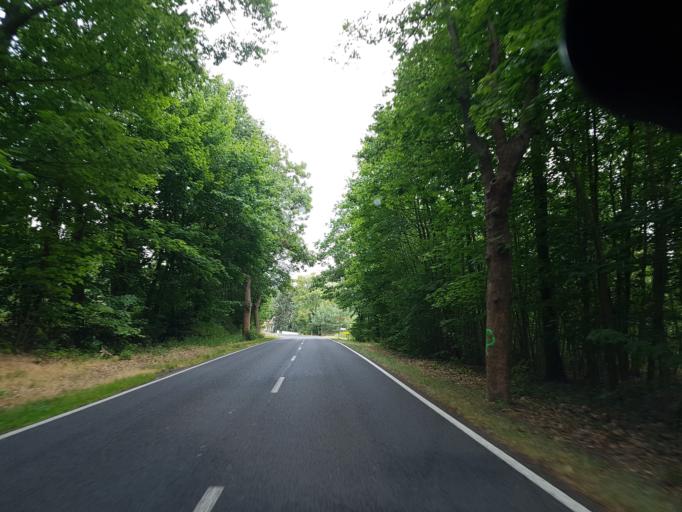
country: DE
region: Brandenburg
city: Sallgast
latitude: 51.5808
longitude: 13.8487
